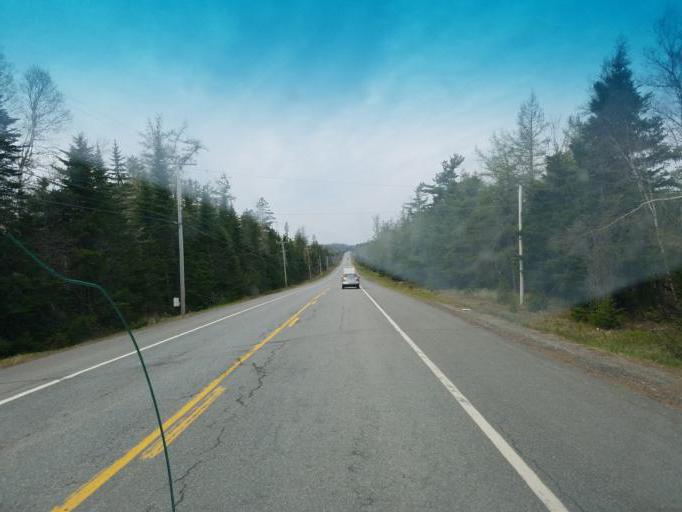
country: US
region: Maine
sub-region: Washington County
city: East Machias
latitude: 44.7547
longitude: -67.2369
